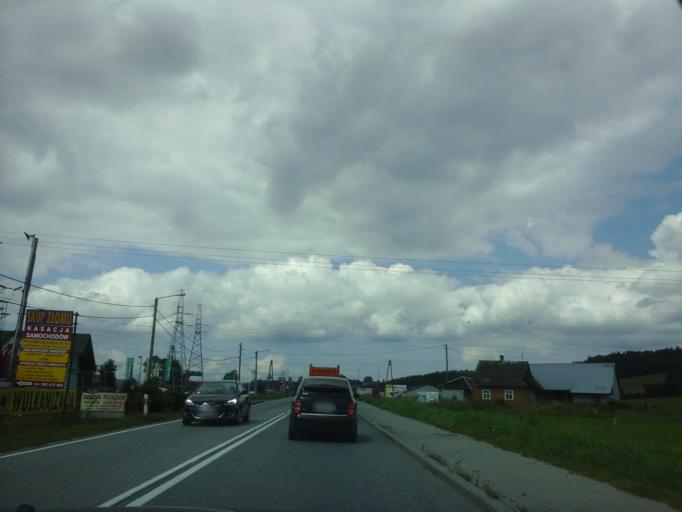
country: PL
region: Lesser Poland Voivodeship
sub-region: Powiat suski
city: Jordanow
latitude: 49.6537
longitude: 19.8182
